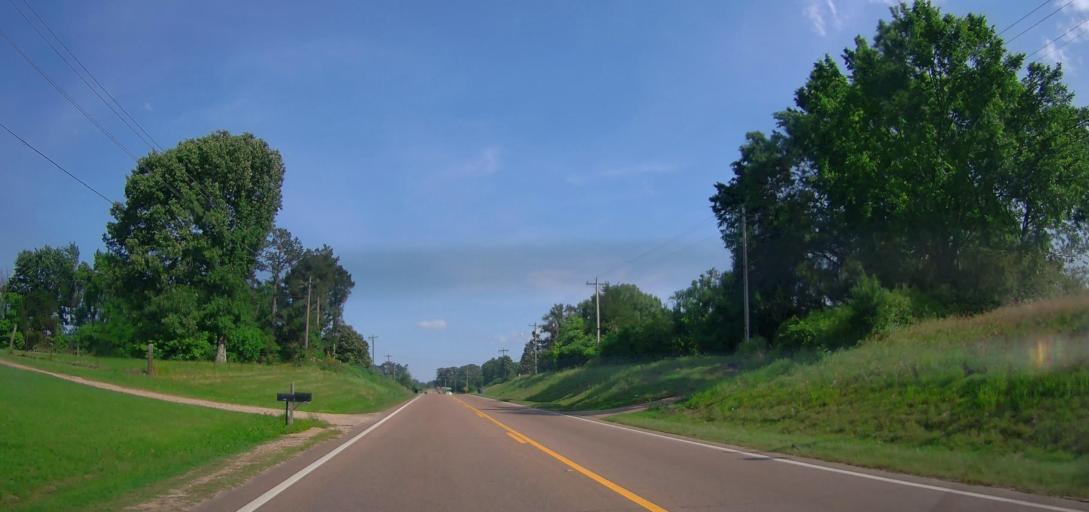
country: US
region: Mississippi
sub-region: De Soto County
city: Olive Branch
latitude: 34.9858
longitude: -89.8610
